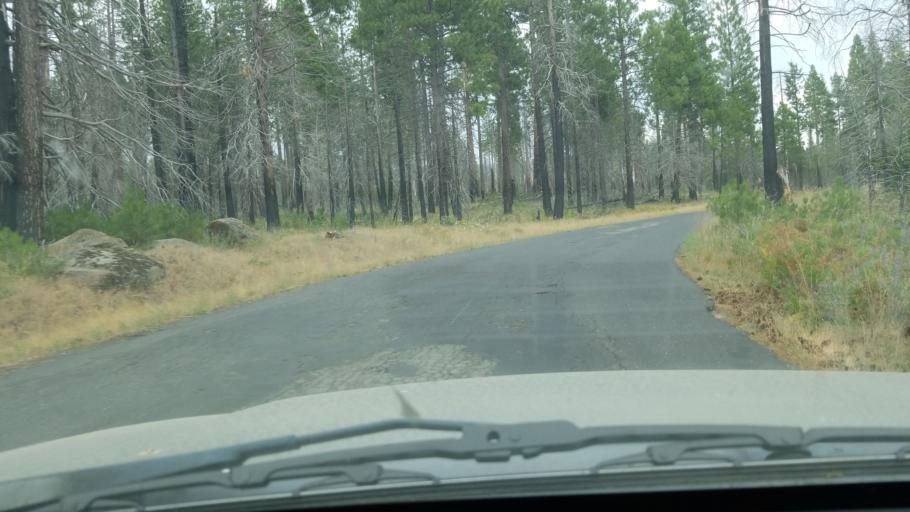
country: US
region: California
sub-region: Mariposa County
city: Yosemite Valley
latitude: 37.8389
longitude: -119.8501
